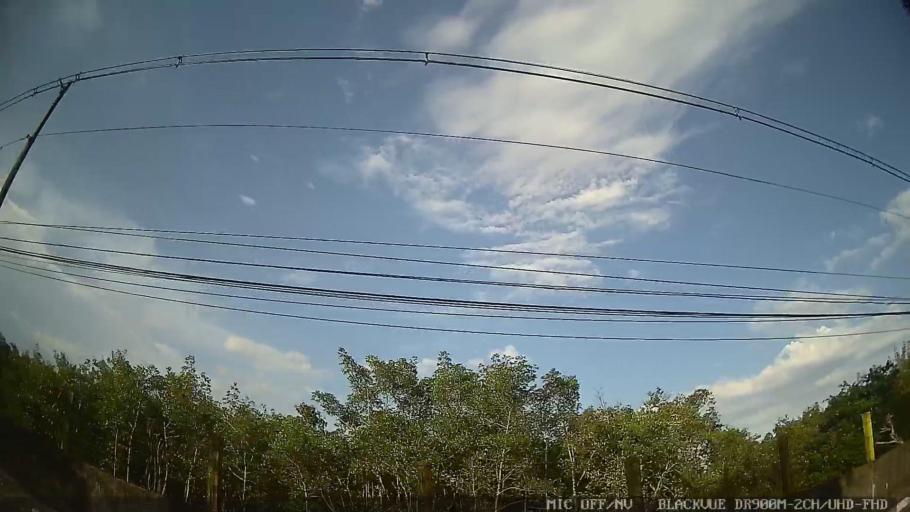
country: BR
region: Sao Paulo
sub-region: Cubatao
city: Cubatao
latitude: -23.9050
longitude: -46.4232
